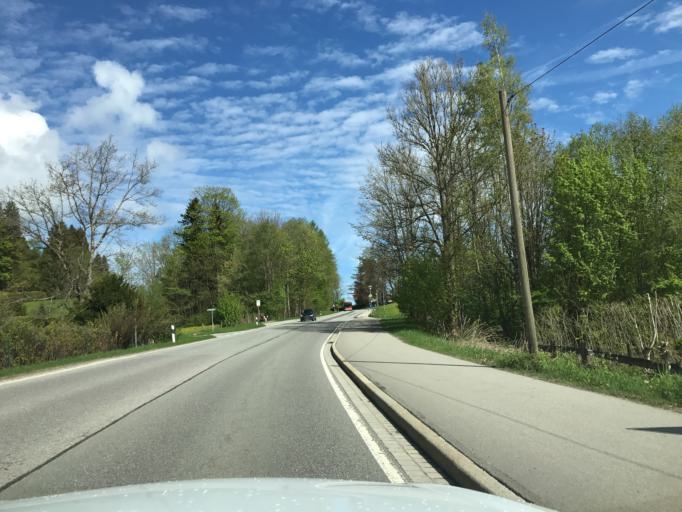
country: DE
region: Bavaria
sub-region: Upper Bavaria
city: Bad Wiessee
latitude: 47.6959
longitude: 11.7323
